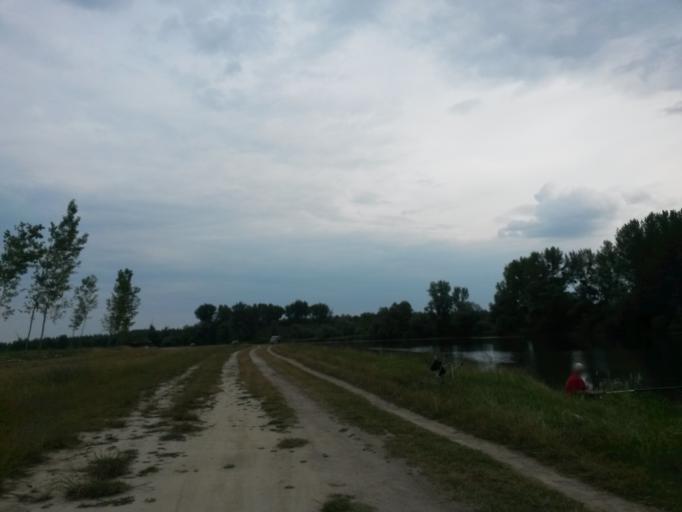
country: HR
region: Osjecko-Baranjska
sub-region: Grad Osijek
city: Bilje
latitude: 45.5890
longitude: 18.7427
